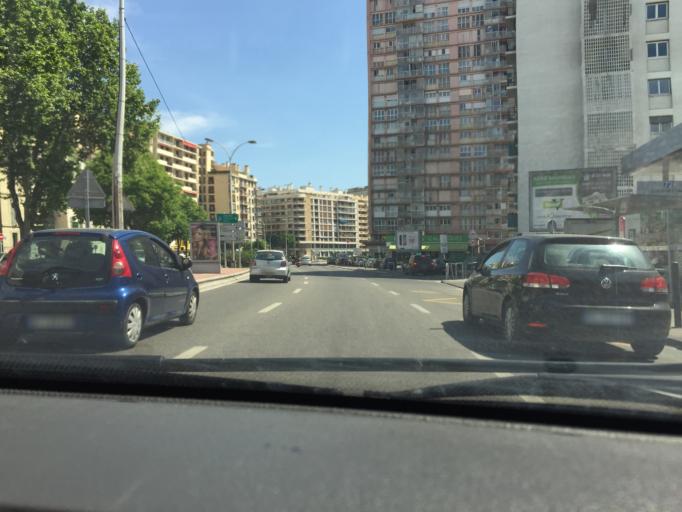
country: FR
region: Provence-Alpes-Cote d'Azur
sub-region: Departement des Bouches-du-Rhone
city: Marseille 05
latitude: 43.2954
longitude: 5.4004
